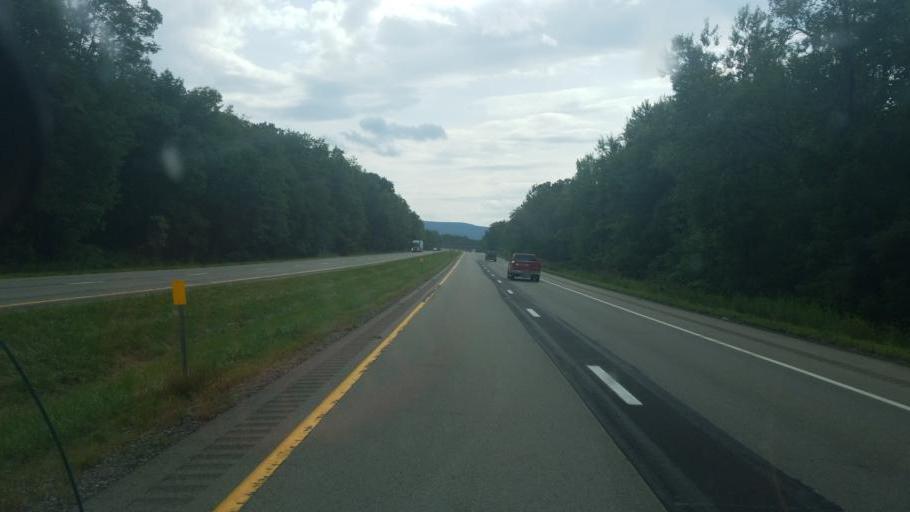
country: US
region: New York
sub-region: Cattaraugus County
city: Salamanca
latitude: 42.1416
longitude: -78.7724
